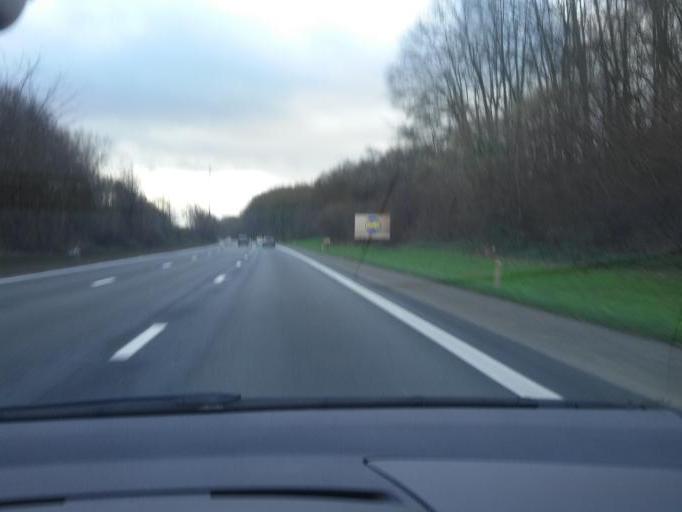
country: BE
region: Flanders
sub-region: Provincie Vlaams-Brabant
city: Overijse
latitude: 50.7637
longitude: 4.5072
